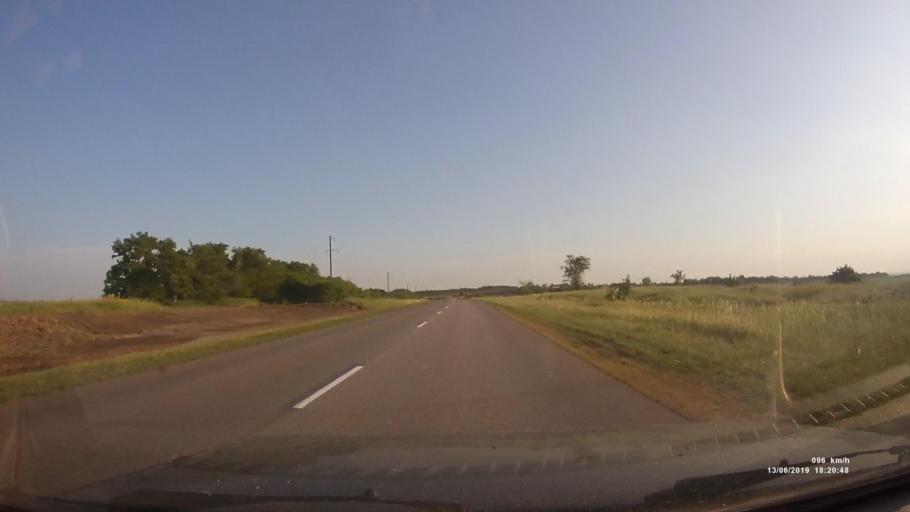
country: RU
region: Rostov
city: Kazanskaya
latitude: 49.8790
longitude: 41.2963
